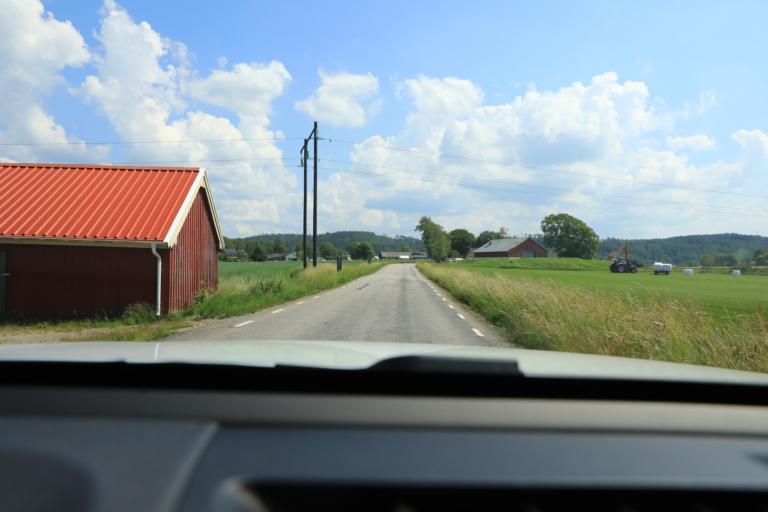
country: SE
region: Halland
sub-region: Varbergs Kommun
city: Veddige
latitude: 57.2074
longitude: 12.3129
